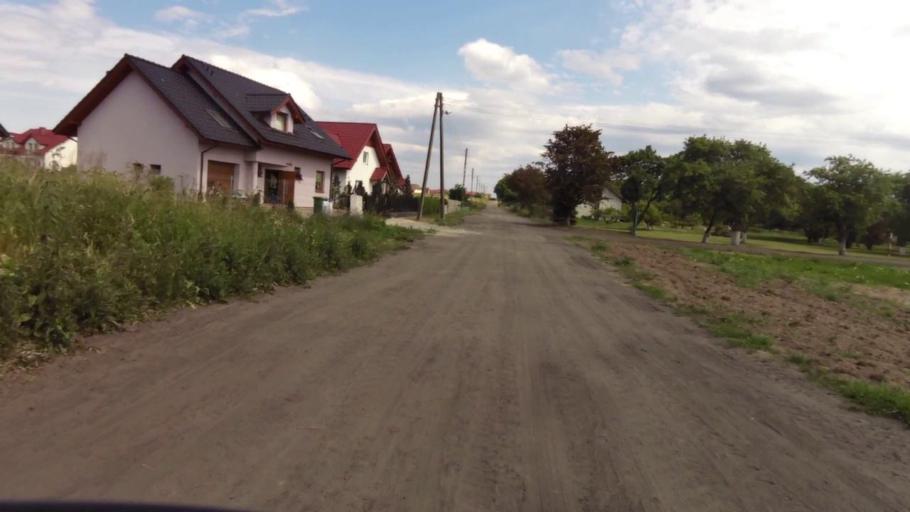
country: PL
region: West Pomeranian Voivodeship
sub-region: Powiat kamienski
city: Wolin
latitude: 53.8438
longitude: 14.6006
